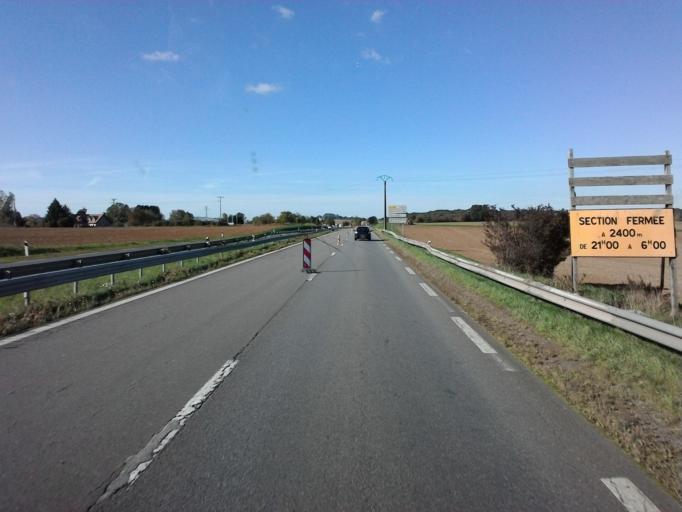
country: FR
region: Lorraine
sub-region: Departement de Meurthe-et-Moselle
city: Haucourt-Moulaine
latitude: 49.4855
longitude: 5.8145
